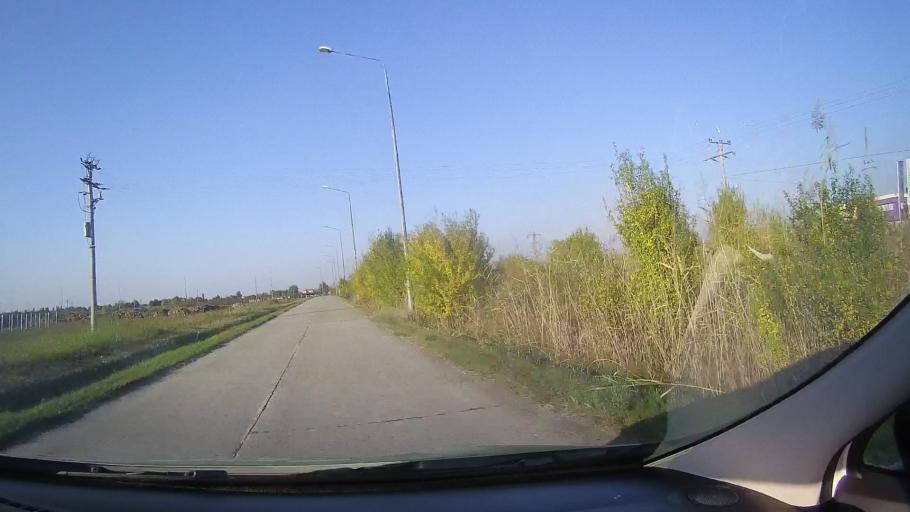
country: RO
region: Bihor
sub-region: Comuna Bors
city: Santion
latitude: 47.1082
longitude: 21.8315
